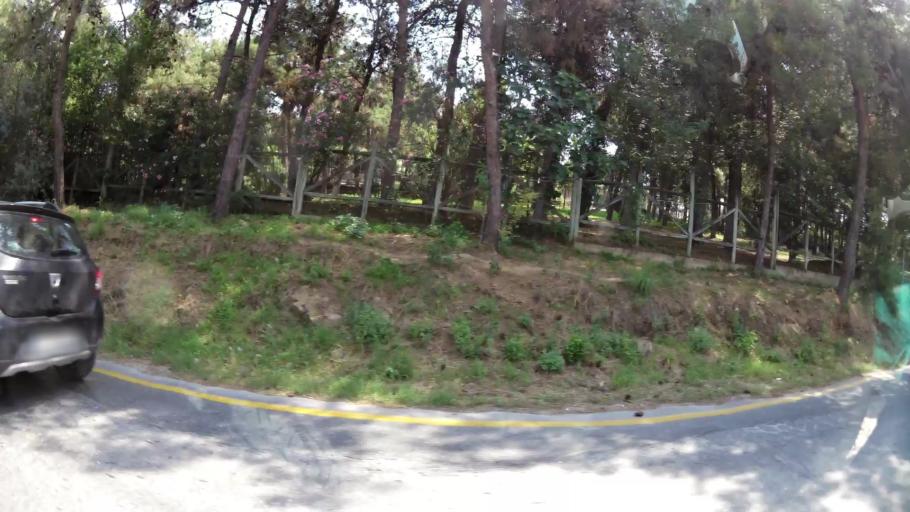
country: GR
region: Central Macedonia
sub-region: Nomos Thessalonikis
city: Agios Pavlos
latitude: 40.6354
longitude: 22.9690
